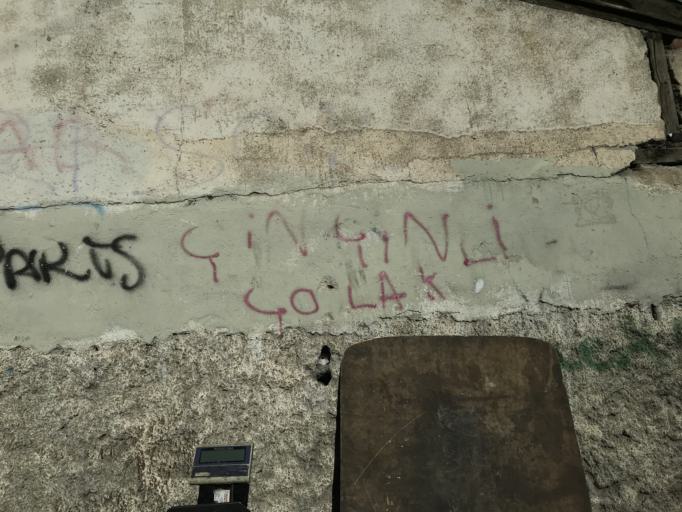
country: TR
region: Ankara
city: Cankaya
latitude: 39.9375
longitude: 32.8694
